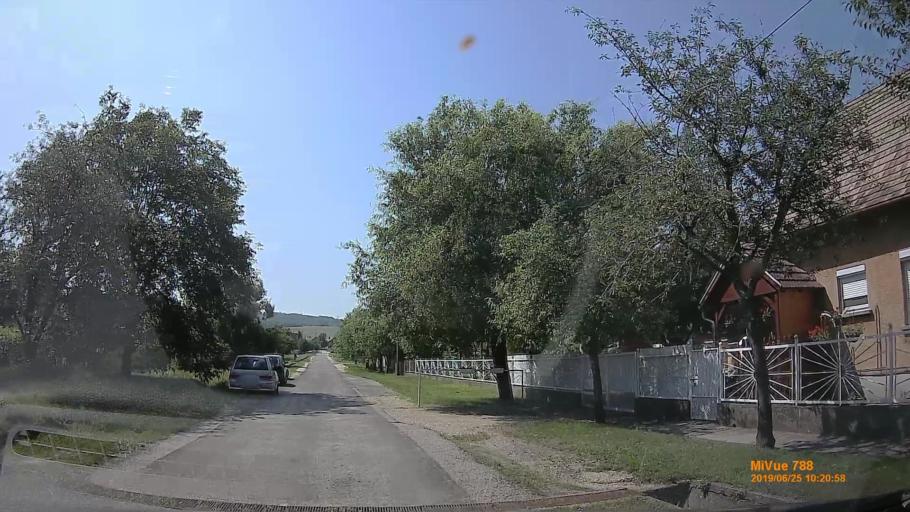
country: HU
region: Komarom-Esztergom
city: Dorog
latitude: 47.7365
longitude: 18.6994
